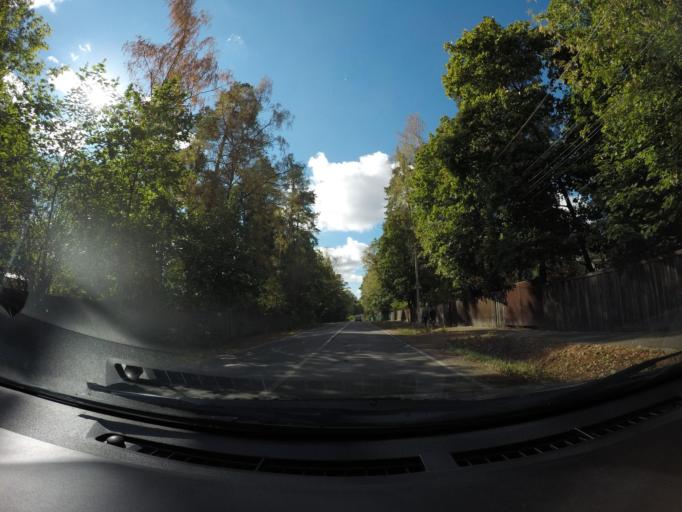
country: RU
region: Moskovskaya
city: Il'inskiy
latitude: 55.6107
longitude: 38.1370
